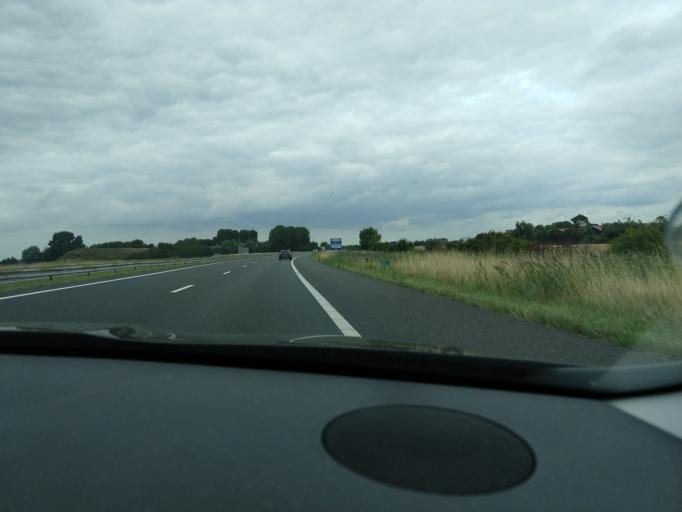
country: NL
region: Zeeland
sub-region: Gemeente Middelburg
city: Middelburg
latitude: 51.4684
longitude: 3.6159
